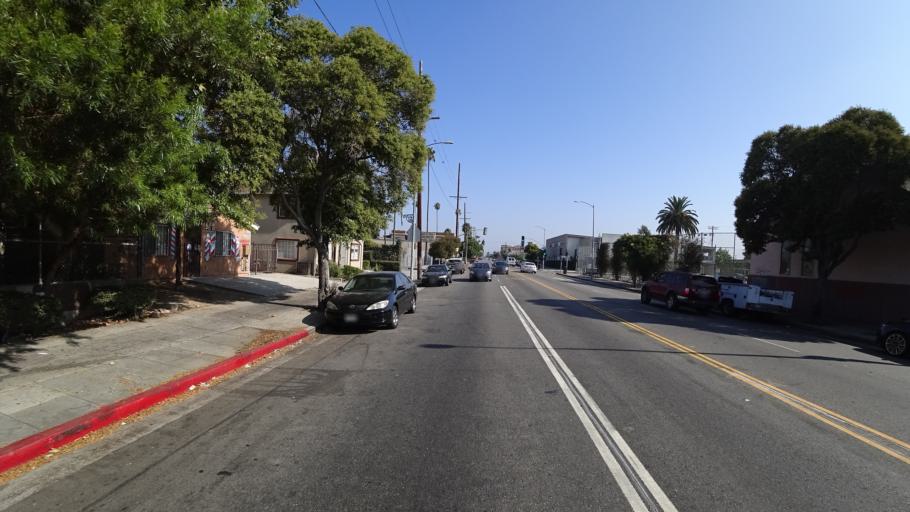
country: US
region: California
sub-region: Los Angeles County
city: Westmont
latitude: 33.9909
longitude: -118.2916
